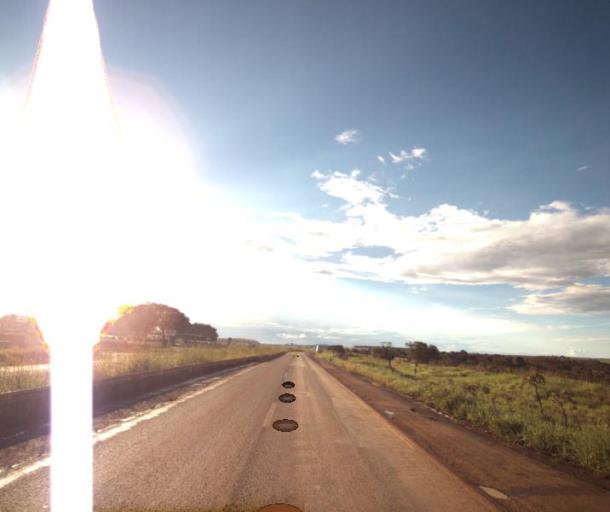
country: BR
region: Goias
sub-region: Anapolis
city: Anapolis
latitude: -16.2560
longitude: -48.9906
